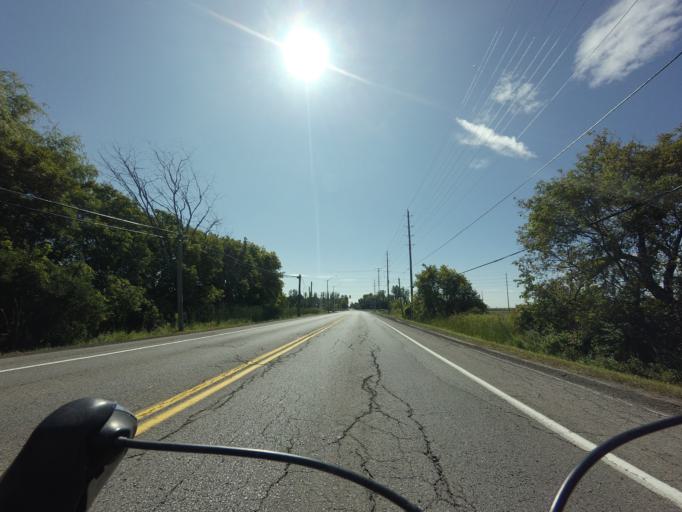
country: CA
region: Ontario
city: Bells Corners
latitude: 45.2608
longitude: -75.8263
